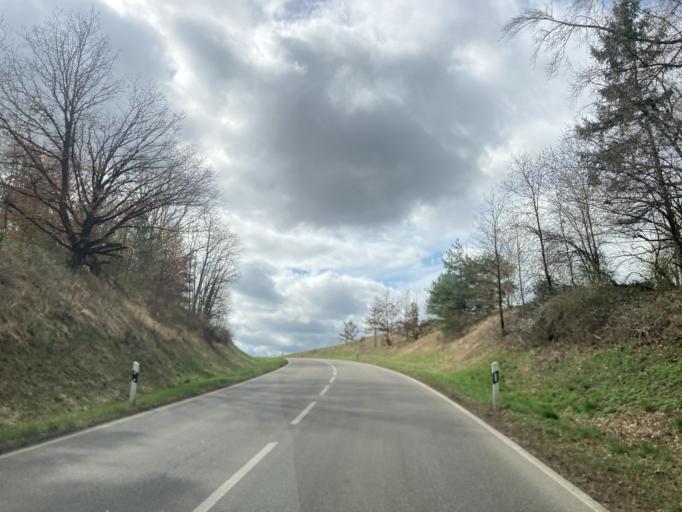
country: DE
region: Baden-Wuerttemberg
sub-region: Regierungsbezirk Stuttgart
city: Bondorf
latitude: 48.5178
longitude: 8.8690
